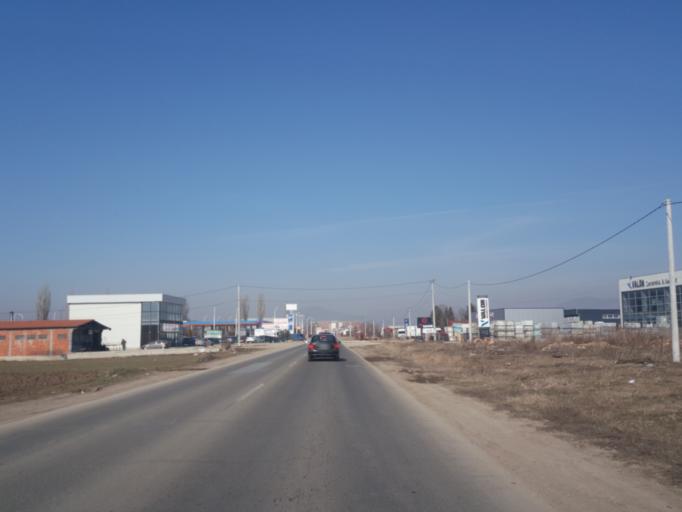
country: XK
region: Mitrovica
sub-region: Vushtrri
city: Vushtrri
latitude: 42.8073
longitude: 20.9895
